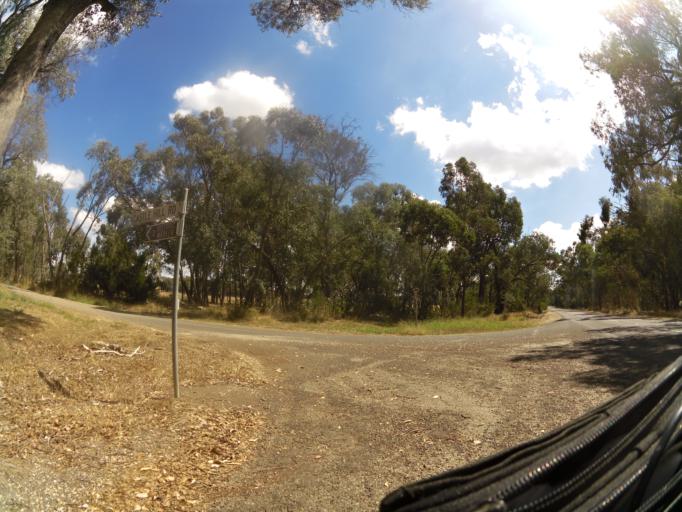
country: AU
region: Victoria
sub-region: Benalla
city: Benalla
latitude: -36.7131
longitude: 146.0442
